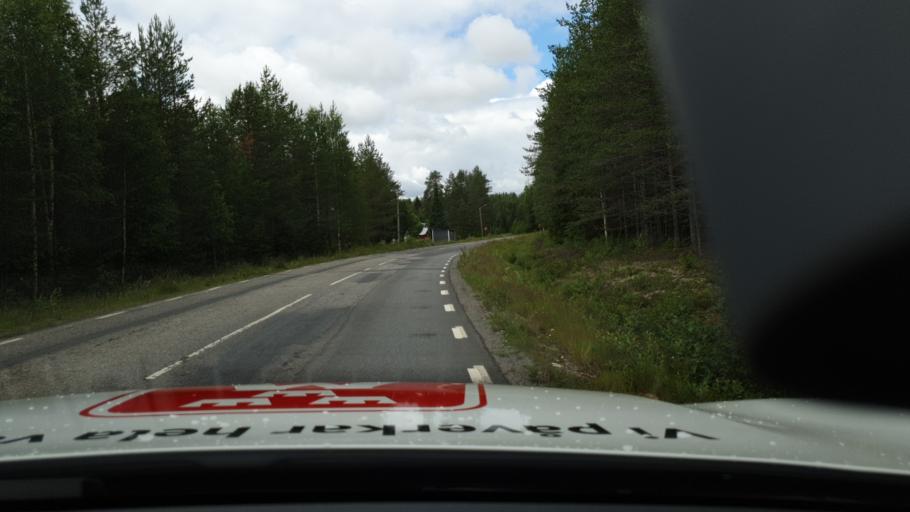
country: SE
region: Norrbotten
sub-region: Bodens Kommun
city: Saevast
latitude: 65.6033
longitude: 21.7257
